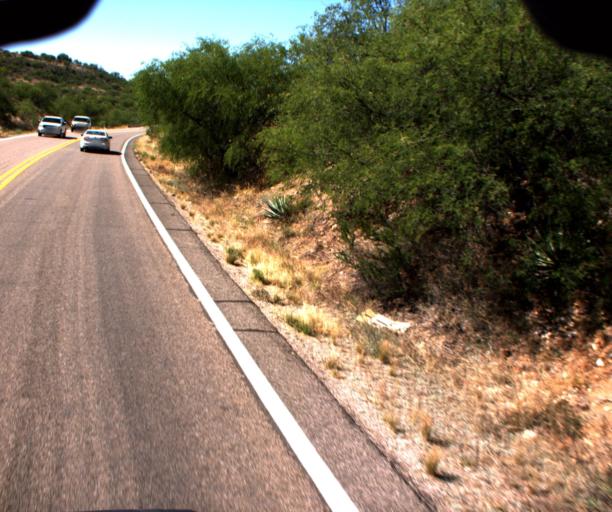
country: US
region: Arizona
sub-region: Santa Cruz County
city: Rio Rico
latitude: 31.5019
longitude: -110.8092
